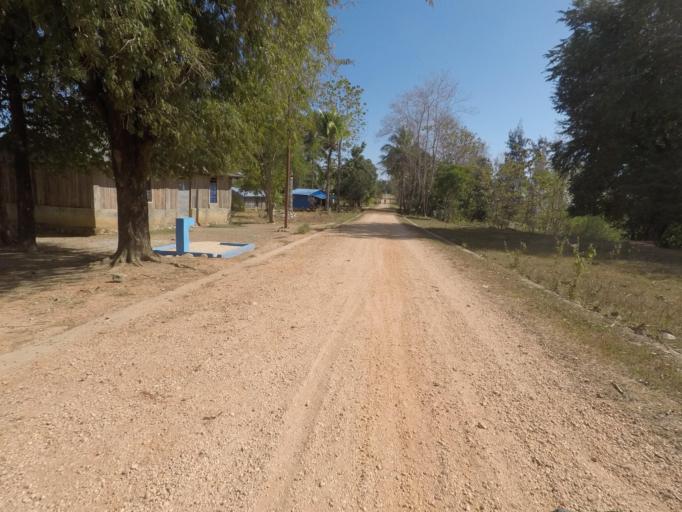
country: TL
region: Bobonaro
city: Maliana
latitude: -8.9567
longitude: 125.2181
